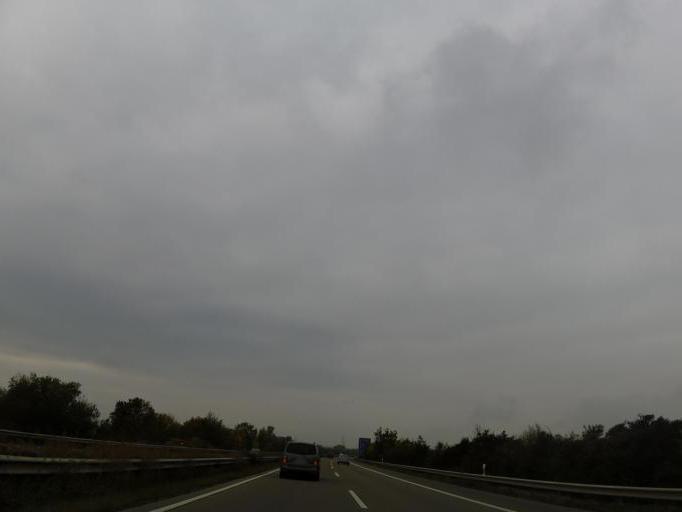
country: DE
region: Rheinland-Pfalz
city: Albig
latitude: 49.7879
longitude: 8.1344
